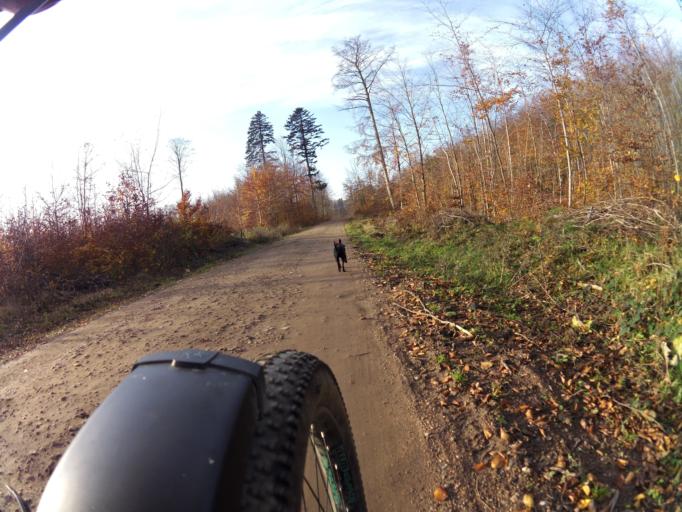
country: PL
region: Pomeranian Voivodeship
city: Strzelno
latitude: 54.7393
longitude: 18.2690
